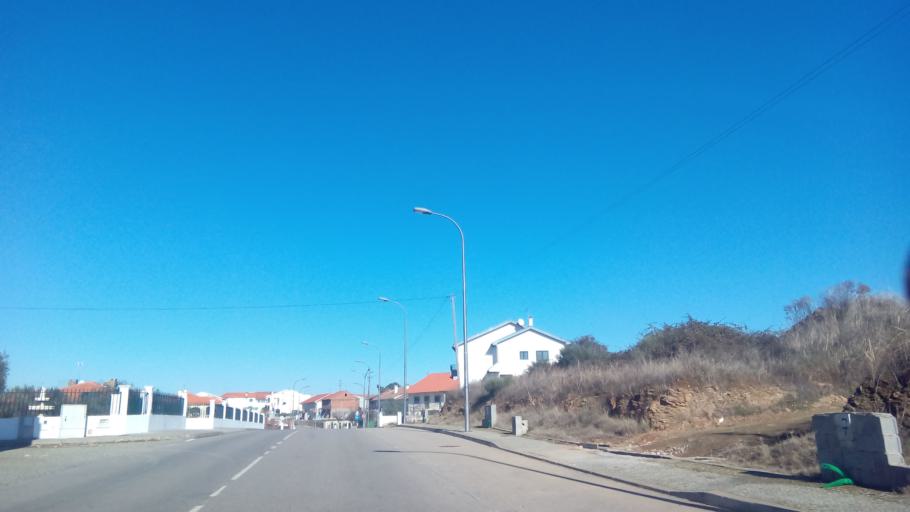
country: PT
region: Braganca
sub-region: Vimioso
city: Vimioso
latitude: 41.6347
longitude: -6.6026
